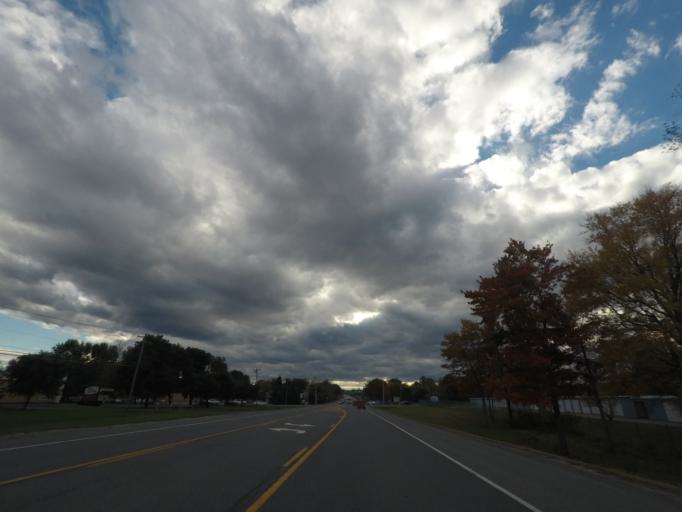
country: US
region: New York
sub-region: Albany County
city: Colonie
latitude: 42.7294
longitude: -73.8550
